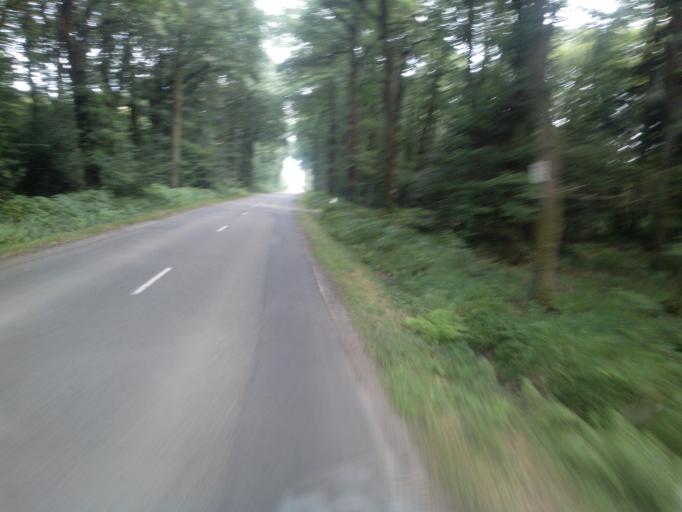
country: FR
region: Brittany
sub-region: Departement d'Ille-et-Vilaine
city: Maxent
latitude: 47.9862
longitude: -2.0497
